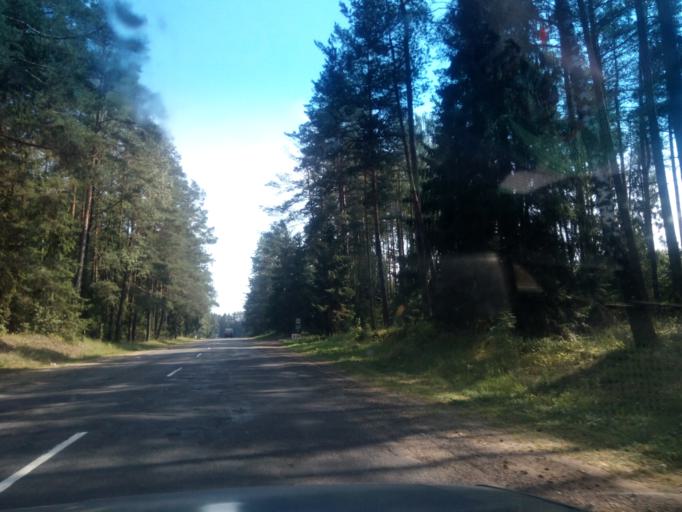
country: BY
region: Vitebsk
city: Vyerkhnyadzvinsk
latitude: 55.7941
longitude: 27.9655
